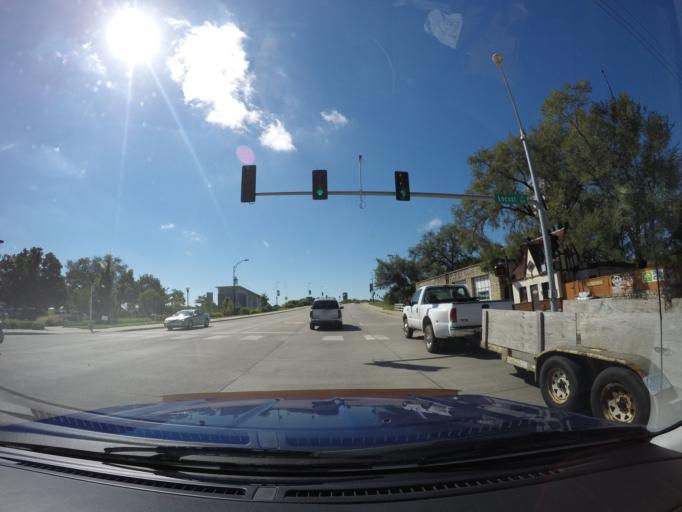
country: US
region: Kansas
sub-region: Douglas County
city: Lawrence
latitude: 38.9778
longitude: -95.2353
